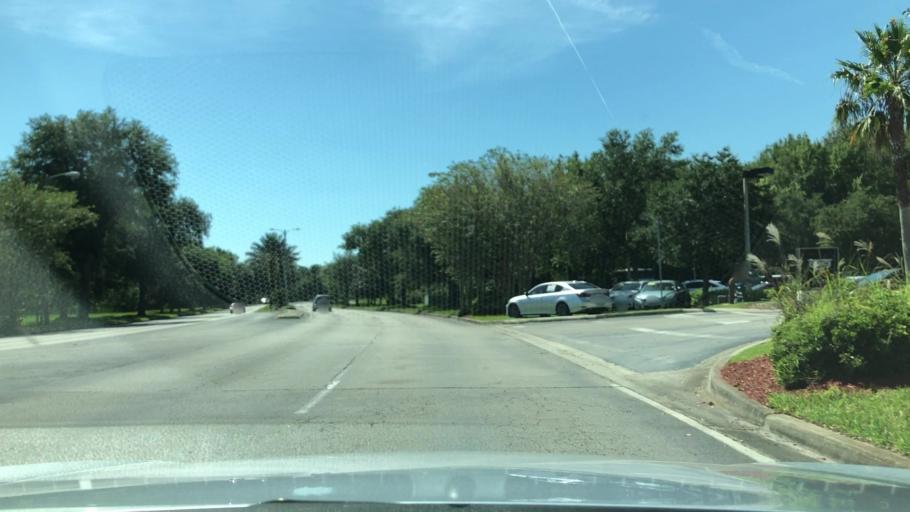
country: US
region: Florida
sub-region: Saint Johns County
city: Saint Augustine
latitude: 29.9233
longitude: -81.4126
